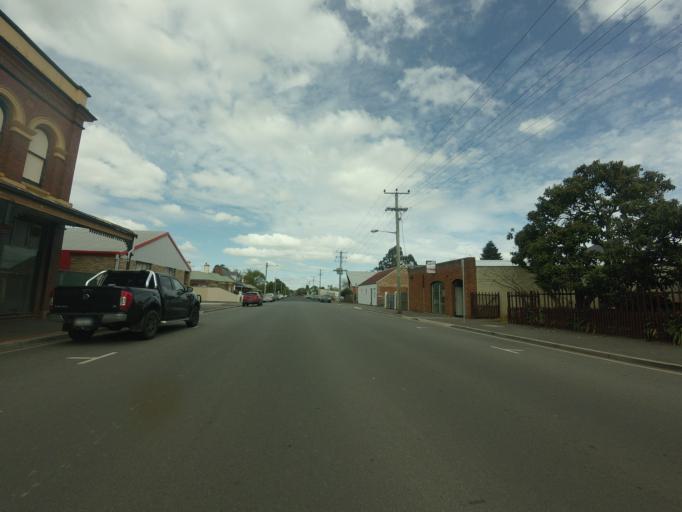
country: AU
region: Tasmania
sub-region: Northern Midlands
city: Longford
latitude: -41.5952
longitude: 147.1224
